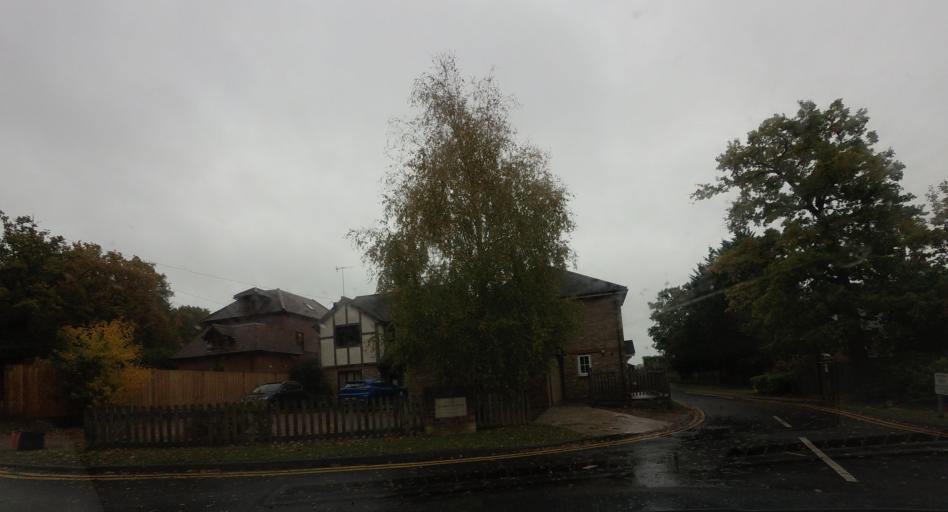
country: GB
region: England
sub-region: Kent
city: Tonbridge
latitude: 51.2208
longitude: 0.2872
